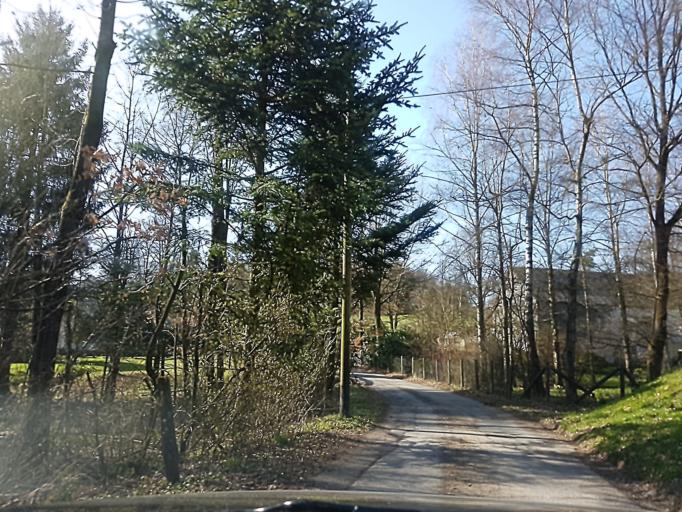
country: DE
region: North Rhine-Westphalia
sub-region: Regierungsbezirk Koln
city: Marienheide
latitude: 51.1199
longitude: 7.5301
